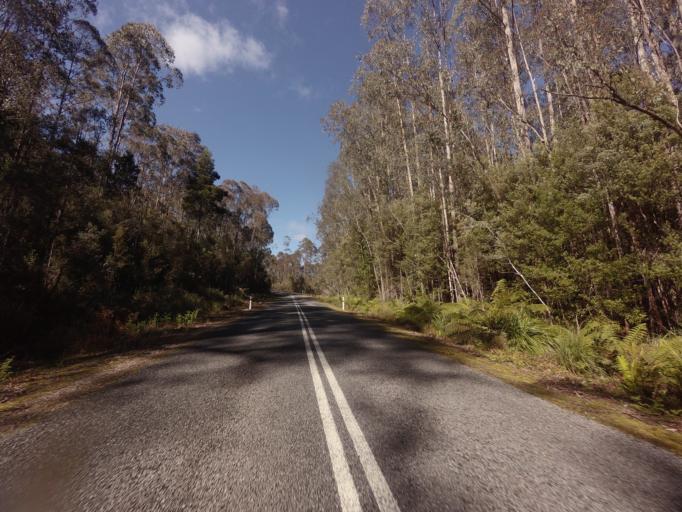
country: AU
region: Tasmania
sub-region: Huon Valley
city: Geeveston
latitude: -42.7790
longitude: 146.3984
